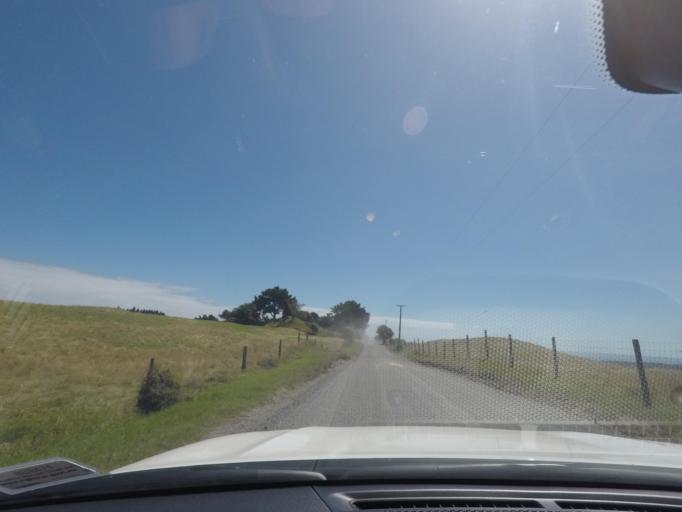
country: NZ
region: Auckland
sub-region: Auckland
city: Parakai
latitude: -36.5855
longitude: 174.2895
